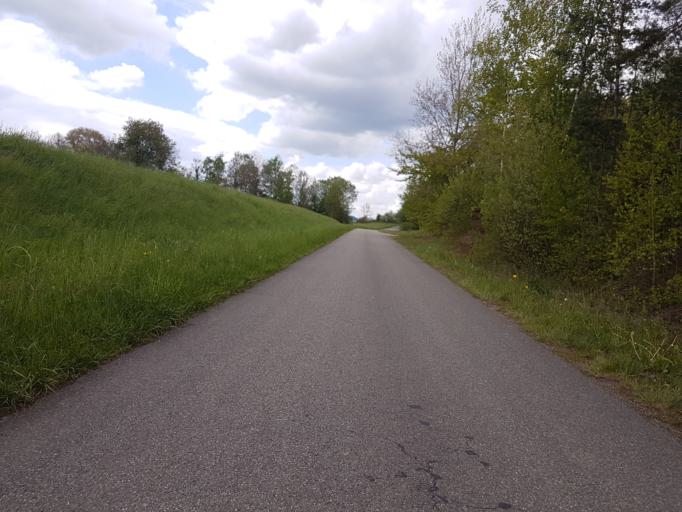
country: CH
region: Solothurn
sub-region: Bezirk Gaeu
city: Wolfwil
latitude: 47.2550
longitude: 7.7813
